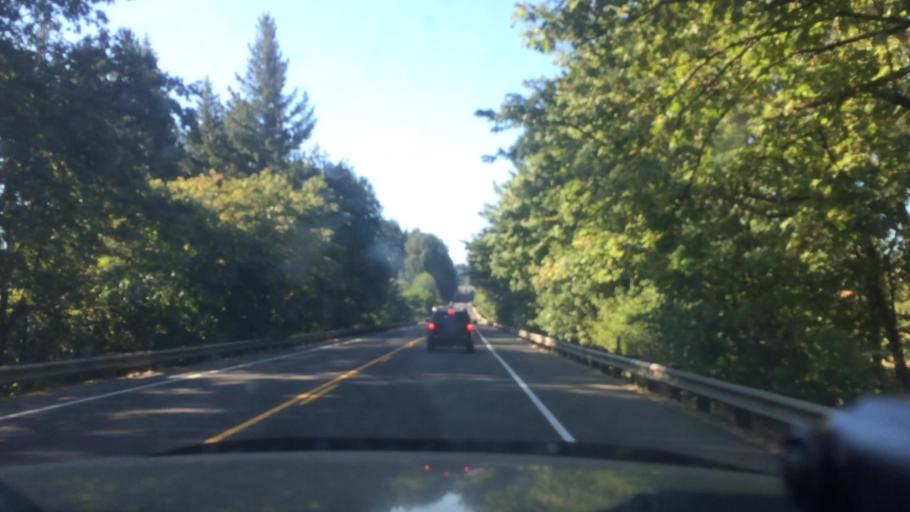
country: US
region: Oregon
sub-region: Yamhill County
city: Newberg
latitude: 45.2695
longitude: -122.9436
